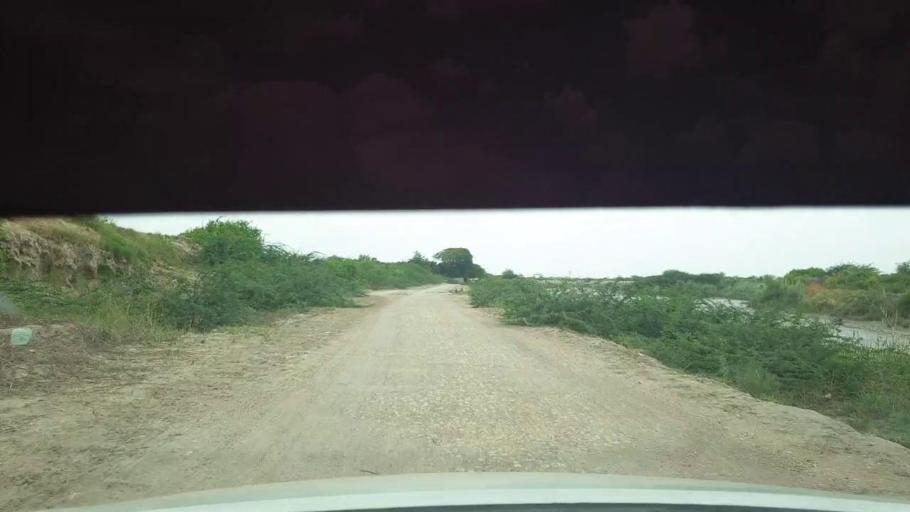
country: PK
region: Sindh
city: Kadhan
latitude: 24.4653
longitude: 69.0487
